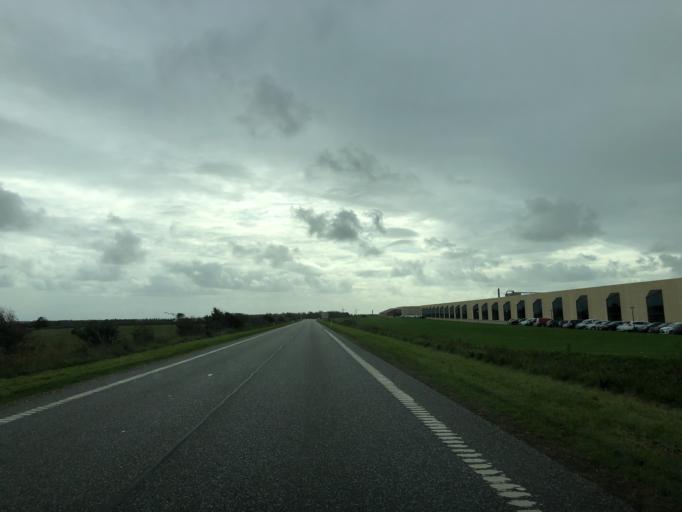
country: DK
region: North Denmark
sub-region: Thisted Kommune
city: Hurup
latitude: 56.7478
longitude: 8.4427
